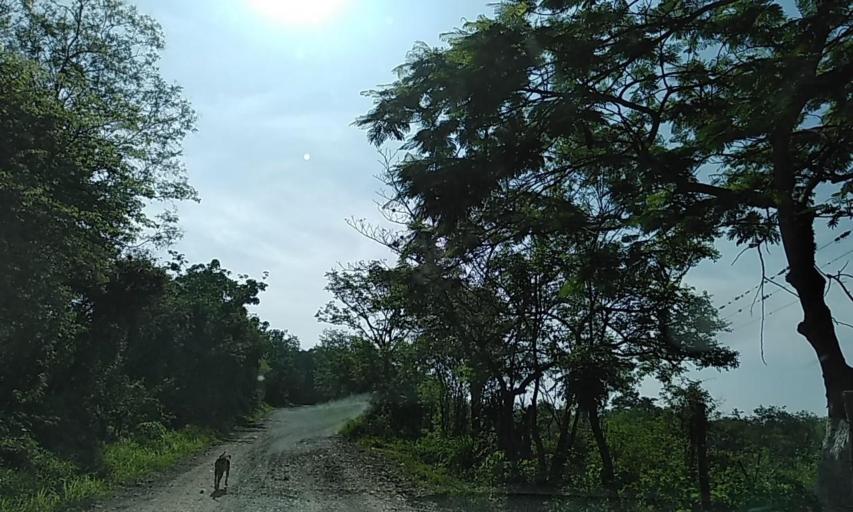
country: MX
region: Veracruz
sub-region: Emiliano Zapata
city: Plan del Rio
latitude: 19.4517
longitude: -96.6833
